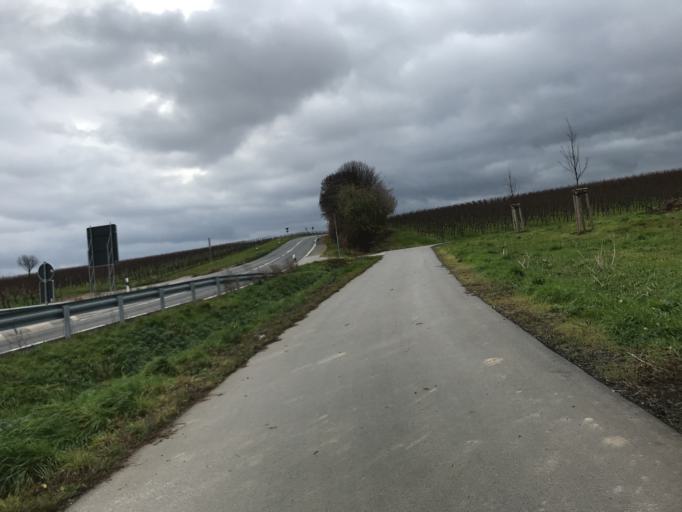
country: DE
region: Rheinland-Pfalz
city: Gau-Bischofsheim
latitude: 49.9194
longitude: 8.2930
